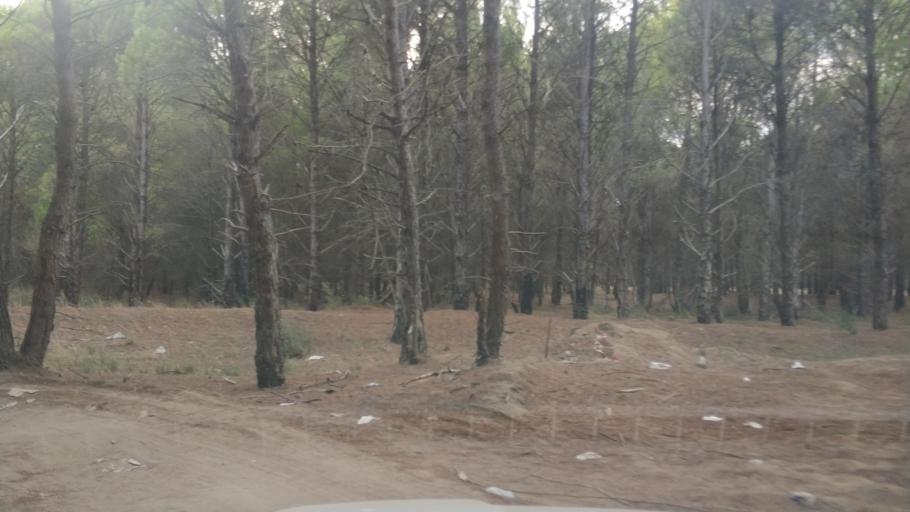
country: AL
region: Vlore
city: Vlore
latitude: 40.5011
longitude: 19.4276
